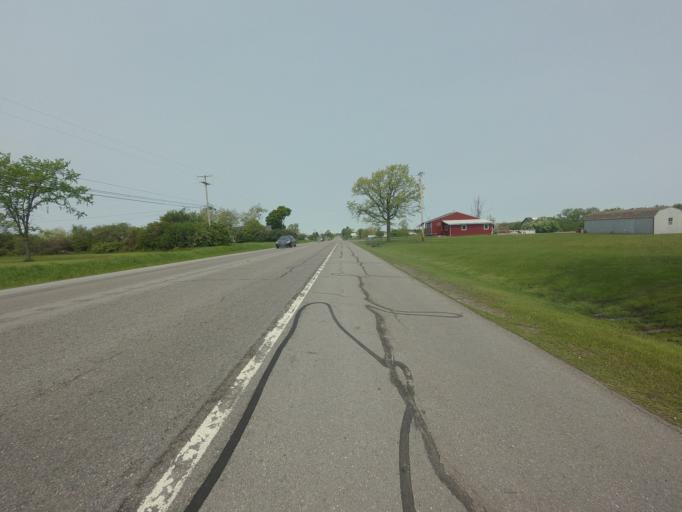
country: US
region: New York
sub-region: Jefferson County
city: Dexter
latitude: 44.0427
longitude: -76.0826
